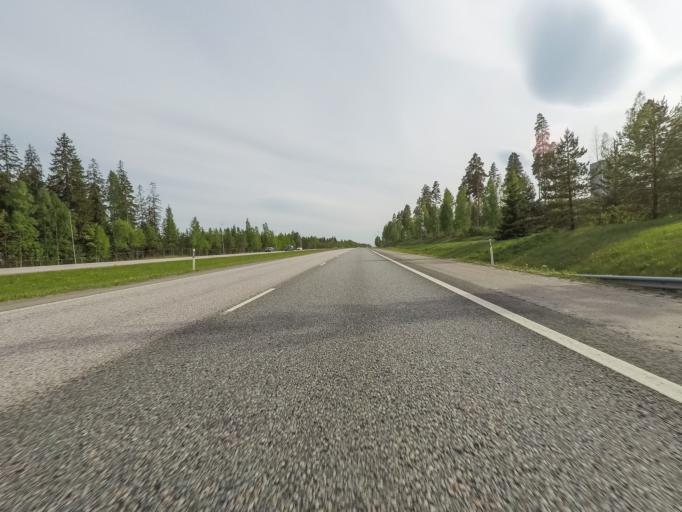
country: FI
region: Uusimaa
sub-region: Helsinki
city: Nurmijaervi
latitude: 60.4537
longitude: 24.8453
